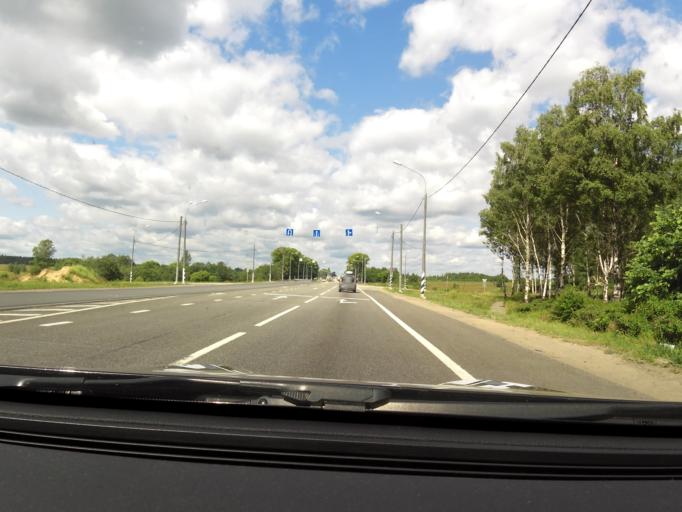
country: RU
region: Tverskaya
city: Likhoslavl'
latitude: 56.9810
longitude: 35.2506
